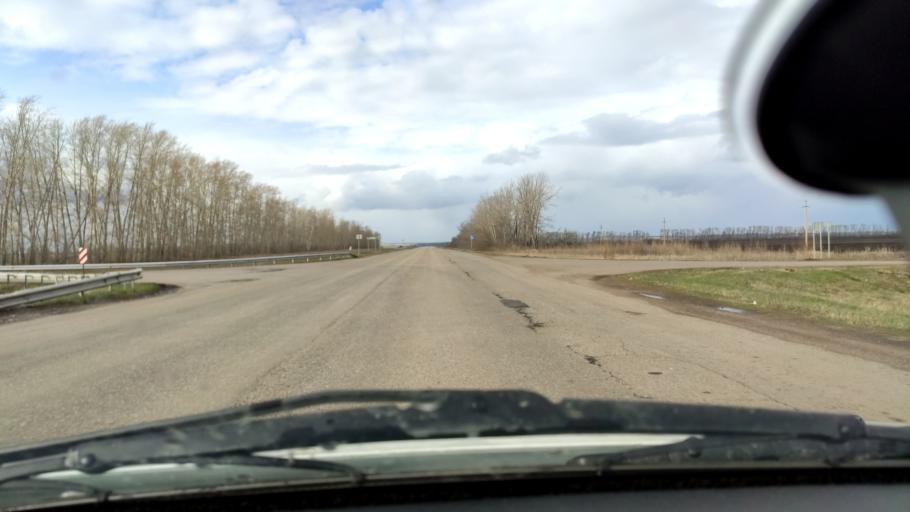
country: RU
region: Bashkortostan
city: Buzdyak
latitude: 54.7083
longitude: 54.5662
